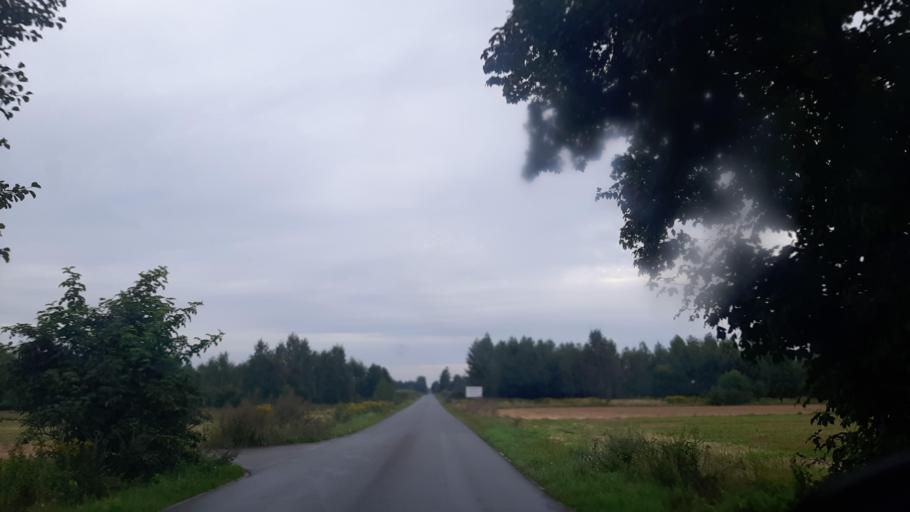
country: PL
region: Lublin Voivodeship
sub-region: Powiat lubartowski
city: Kamionka
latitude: 51.4685
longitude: 22.4356
